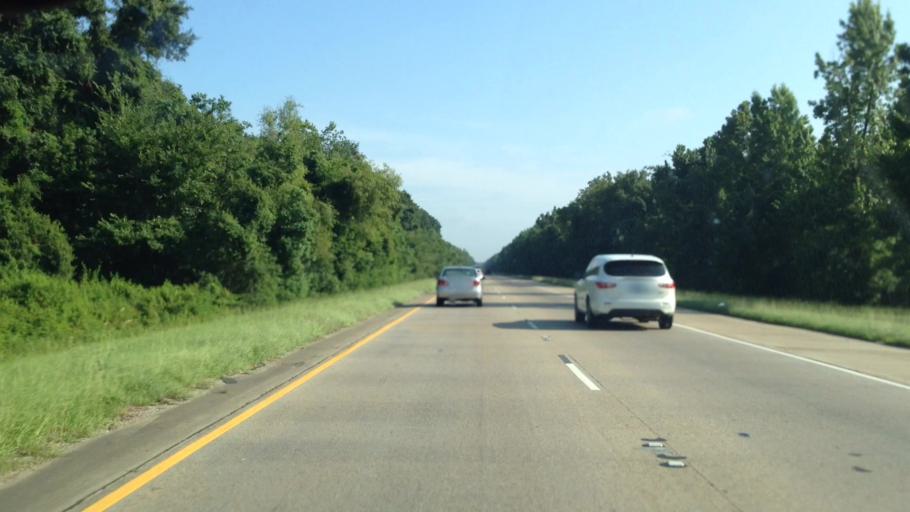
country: US
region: Louisiana
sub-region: Ascension Parish
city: Prairieville
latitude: 30.2853
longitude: -90.9895
